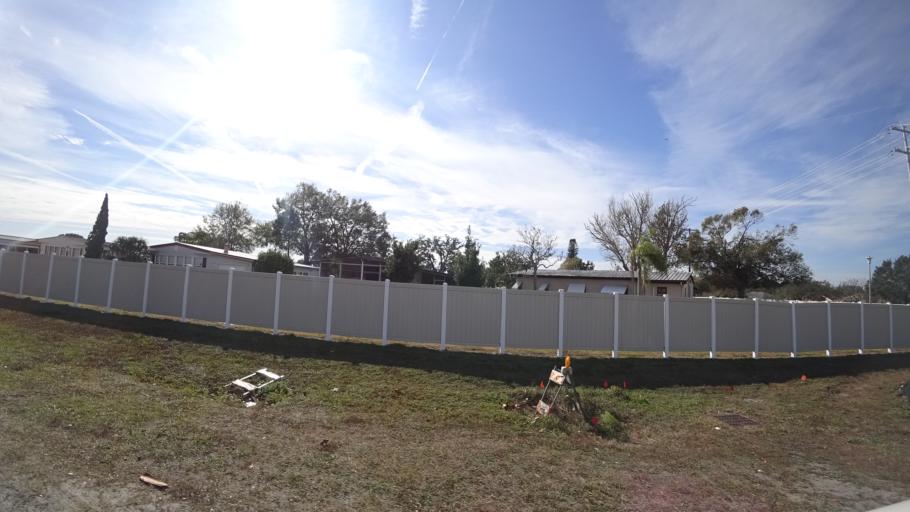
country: US
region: Florida
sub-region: Manatee County
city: Memphis
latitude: 27.5754
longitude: -82.5270
